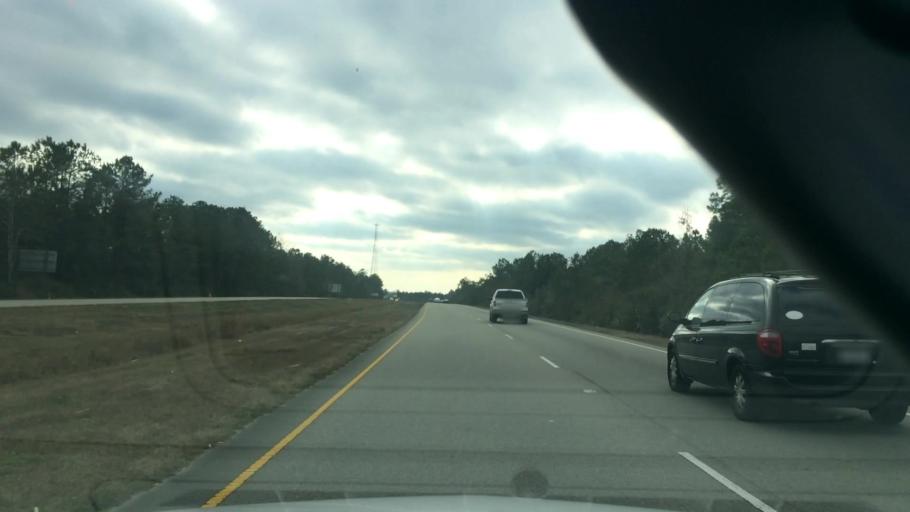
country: US
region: North Carolina
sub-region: Brunswick County
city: Shallotte
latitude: 33.9708
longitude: -78.4111
